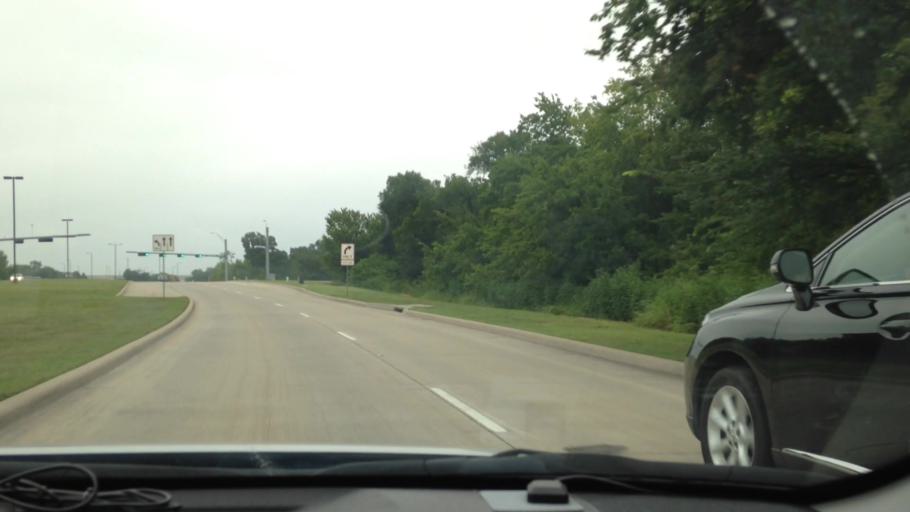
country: US
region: Texas
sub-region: Collin County
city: Allen
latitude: 33.1221
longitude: -96.7175
